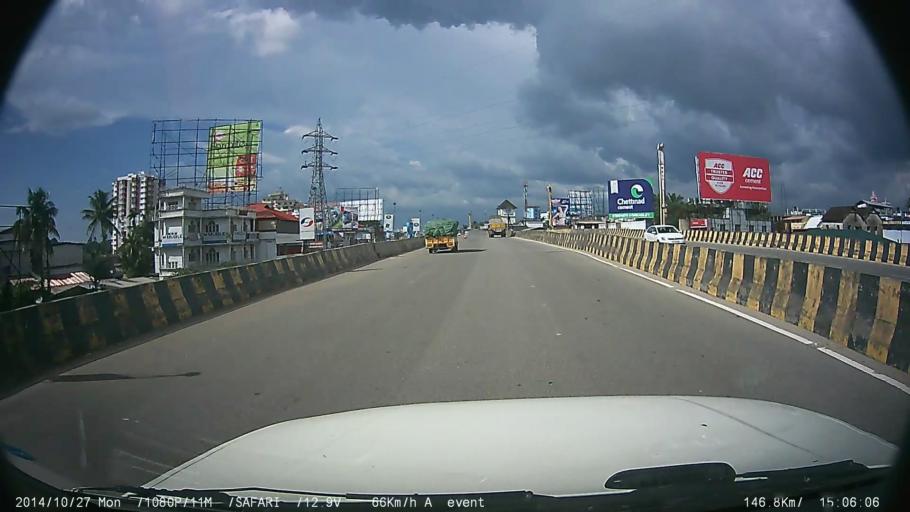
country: IN
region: Kerala
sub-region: Ernakulam
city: Aluva
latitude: 10.1056
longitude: 76.3501
